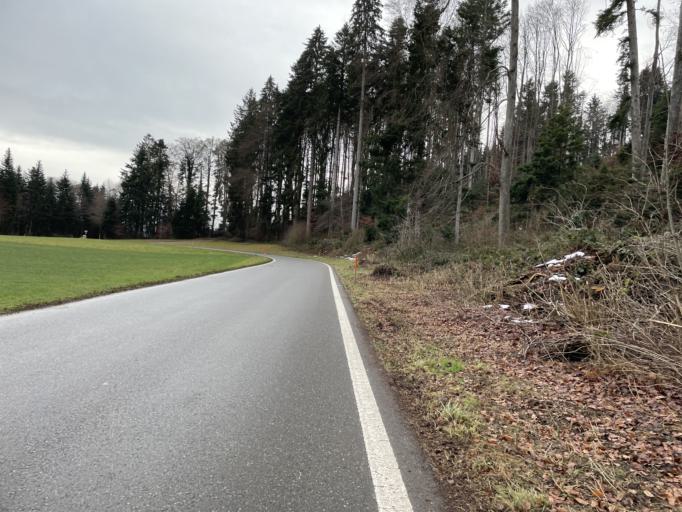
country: CH
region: Bern
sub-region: Bern-Mittelland District
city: Munsingen
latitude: 46.8534
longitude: 7.5434
